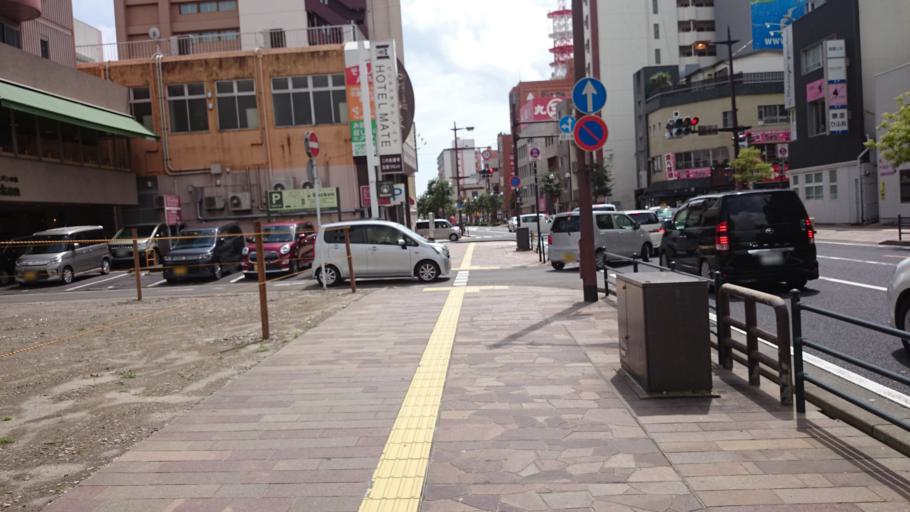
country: JP
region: Kagoshima
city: Kagoshima-shi
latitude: 31.5900
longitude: 130.5570
